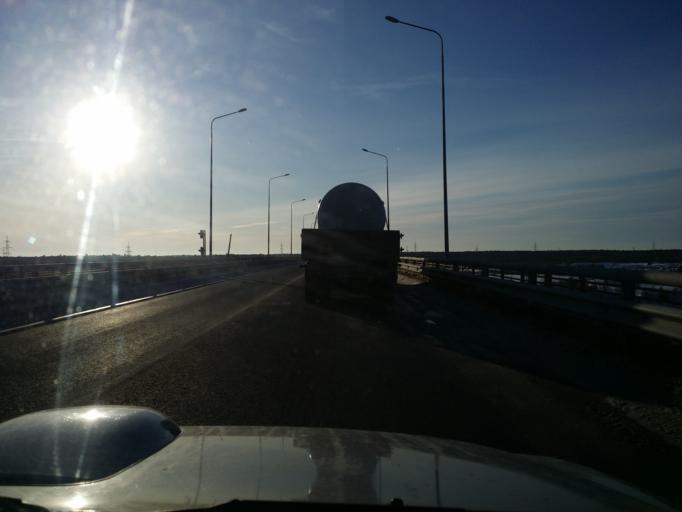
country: RU
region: Khanty-Mansiyskiy Avtonomnyy Okrug
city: Izluchinsk
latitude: 60.9356
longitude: 76.8906
